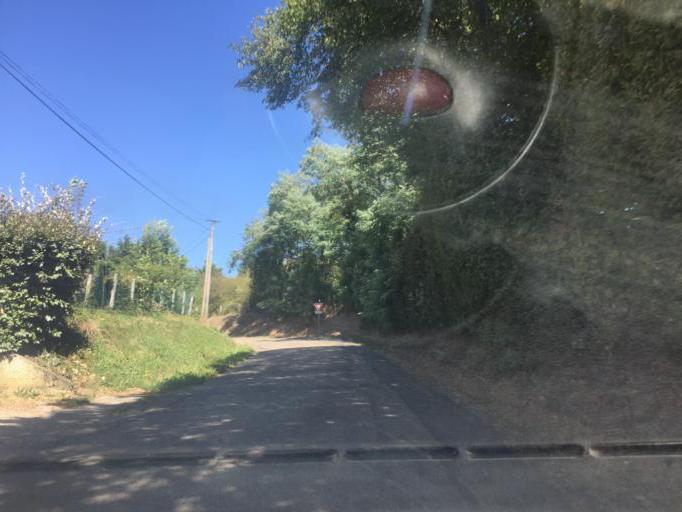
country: FR
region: Rhone-Alpes
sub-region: Departement de l'Ain
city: Tramoyes
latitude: 45.8680
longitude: 4.9756
